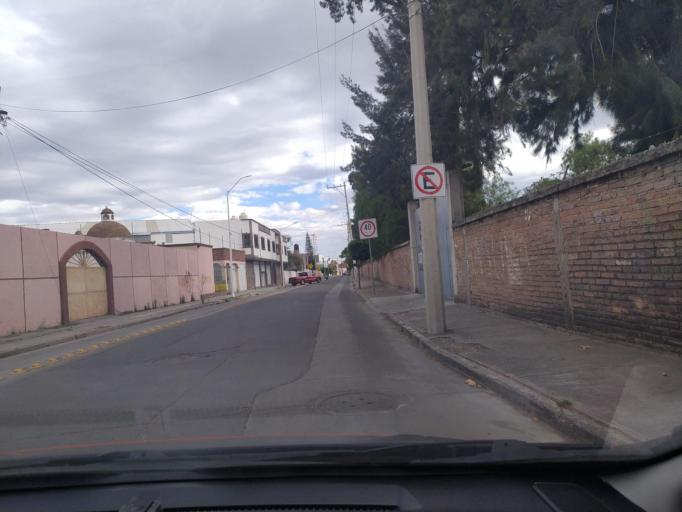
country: LA
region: Oudomxai
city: Muang La
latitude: 21.0213
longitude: 101.8637
